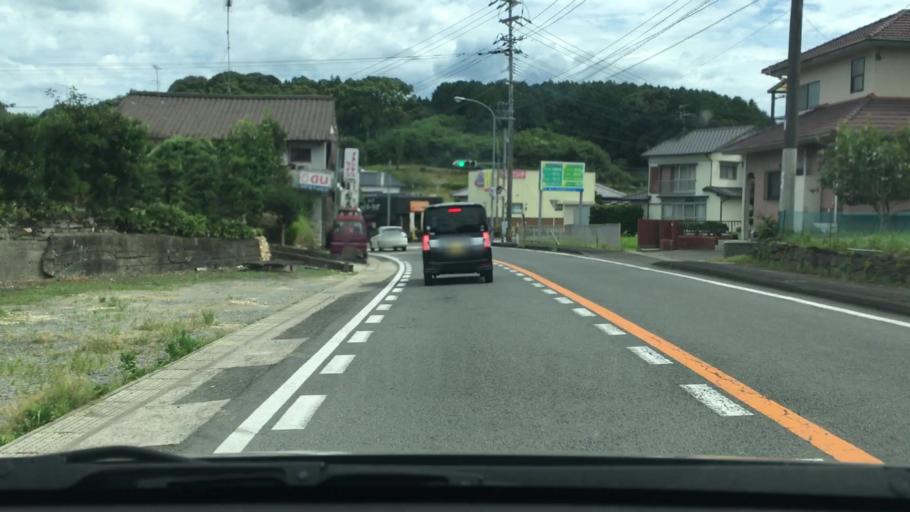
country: JP
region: Nagasaki
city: Togitsu
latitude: 32.9652
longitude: 129.7807
